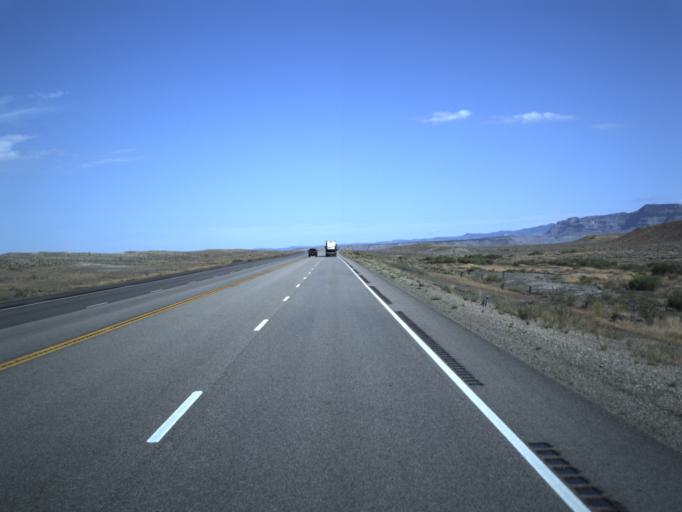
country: US
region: Utah
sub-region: Carbon County
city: East Carbon City
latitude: 39.2976
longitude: -110.3555
